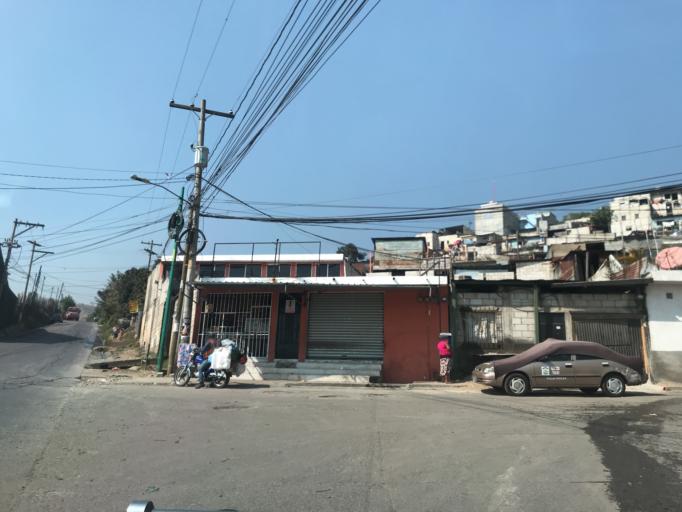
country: GT
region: Guatemala
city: Villa Nueva
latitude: 14.4987
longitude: -90.5875
